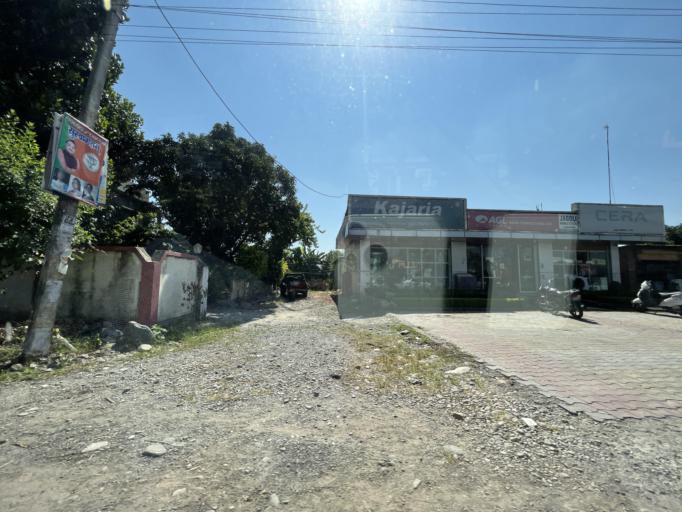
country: IN
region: Uttarakhand
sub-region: Naini Tal
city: Haldwani
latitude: 29.2144
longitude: 79.4793
